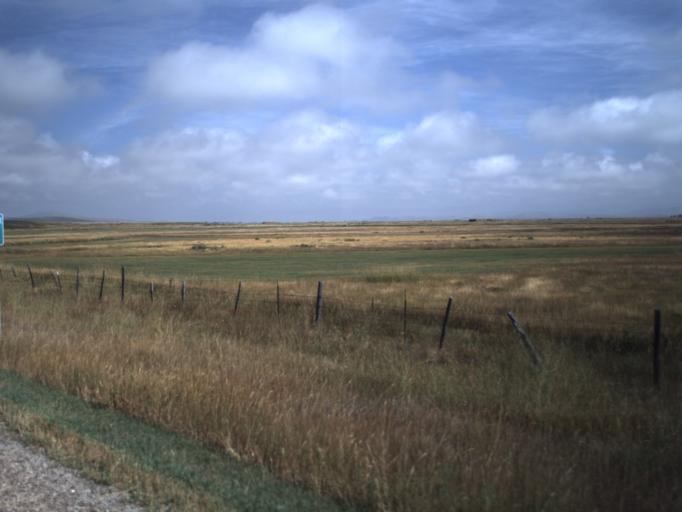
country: US
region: Utah
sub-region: Rich County
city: Randolph
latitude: 41.7193
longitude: -111.1592
